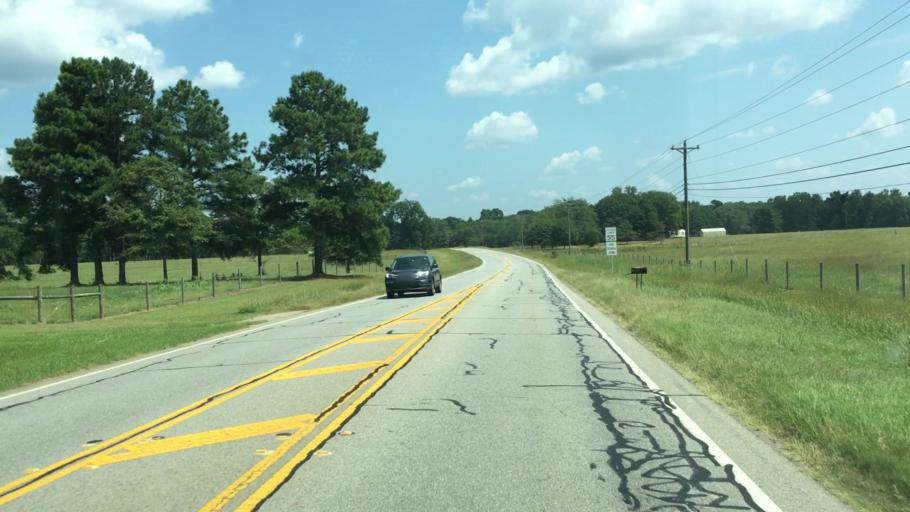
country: US
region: Georgia
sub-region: Oconee County
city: Bogart
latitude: 33.8741
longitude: -83.5237
